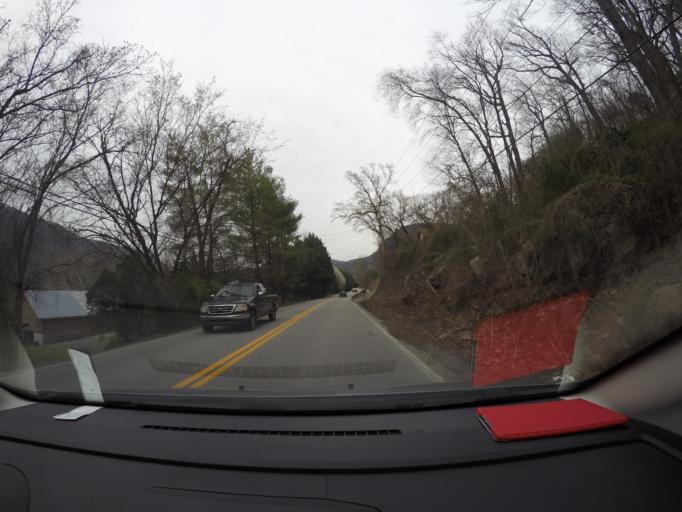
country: US
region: Tennessee
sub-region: Hamilton County
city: Signal Mountain
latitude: 35.1119
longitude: -85.3671
